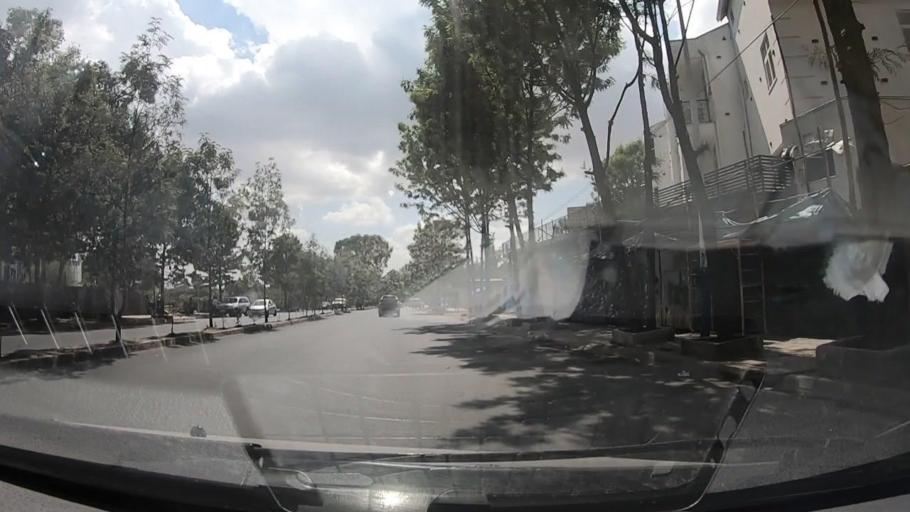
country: ET
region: Adis Abeba
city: Addis Ababa
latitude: 8.9733
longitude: 38.7247
